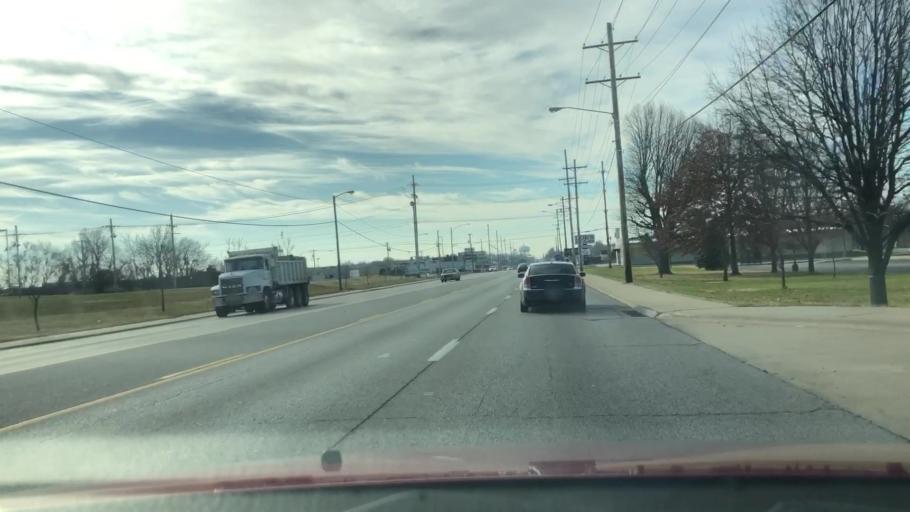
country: US
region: Missouri
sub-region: Greene County
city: Springfield
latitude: 37.2196
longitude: -93.2617
